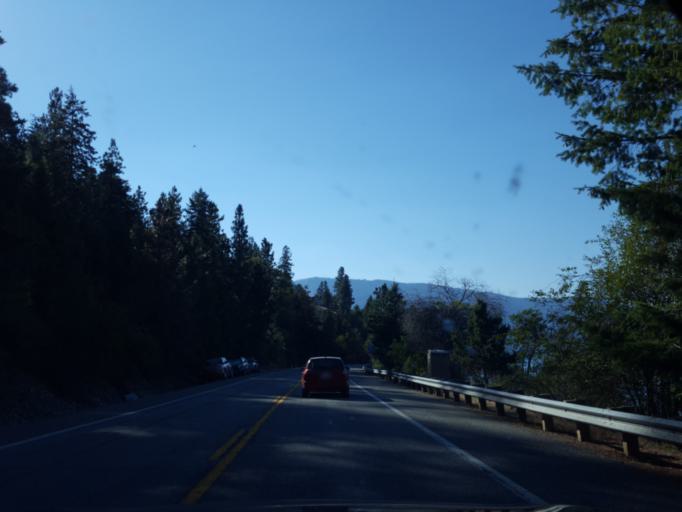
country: US
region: Washington
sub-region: Chelan County
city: Manson
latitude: 47.8562
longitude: -120.1447
